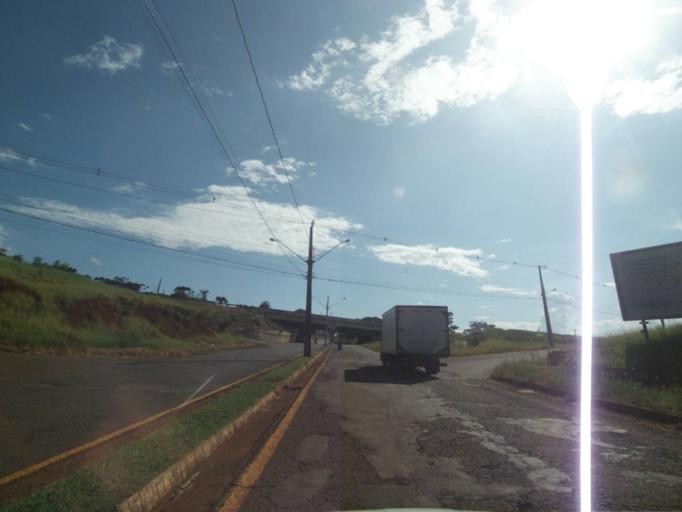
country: BR
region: Parana
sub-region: Londrina
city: Londrina
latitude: -23.3214
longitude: -51.1989
